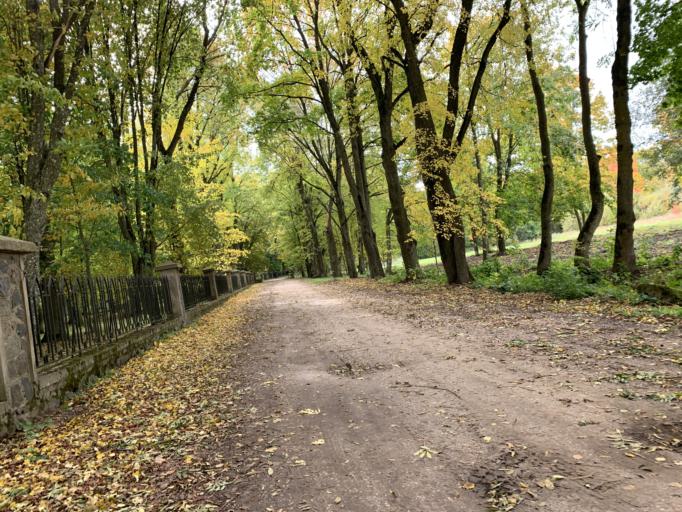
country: BY
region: Minsk
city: Nyasvizh
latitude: 53.2297
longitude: 26.6967
